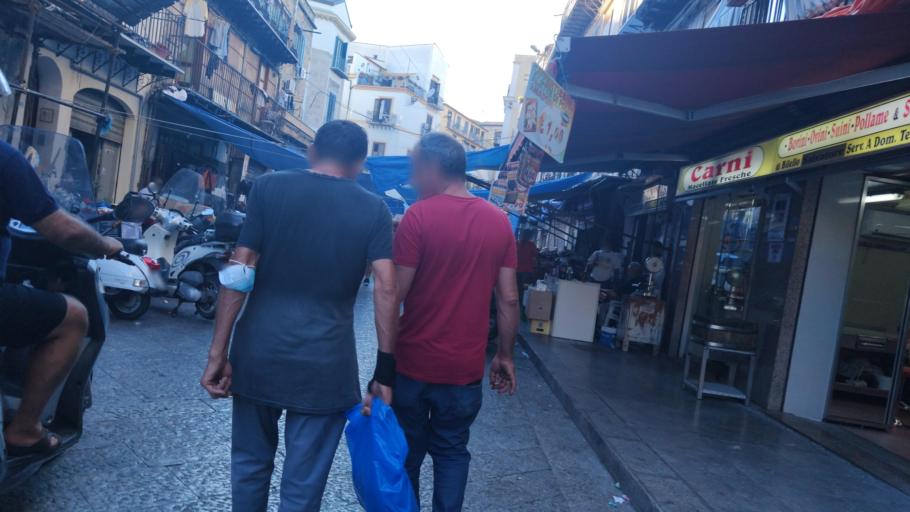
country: IT
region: Sicily
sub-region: Palermo
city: Palermo
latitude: 38.1120
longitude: 13.3606
